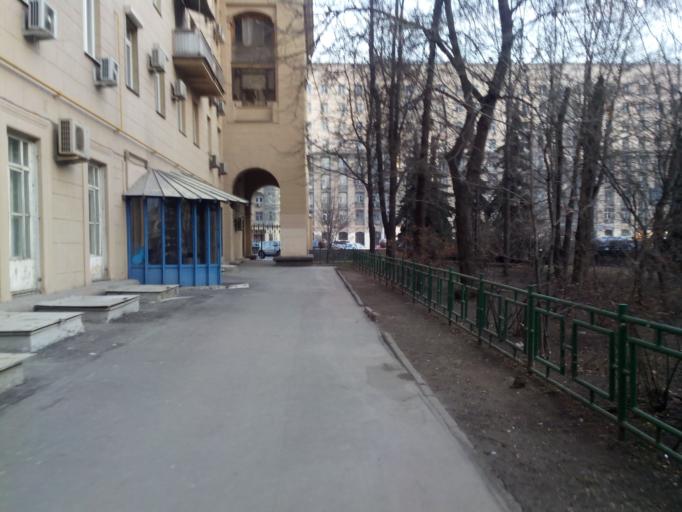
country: RU
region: Moskovskaya
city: Presnenskiy
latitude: 55.7457
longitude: 37.5477
